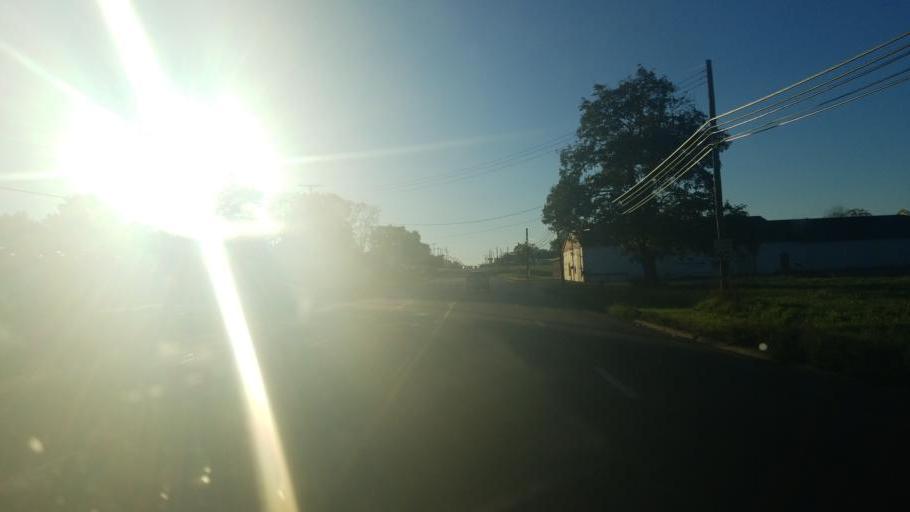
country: US
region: Ohio
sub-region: Stark County
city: Alliance
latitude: 40.9016
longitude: -81.0778
